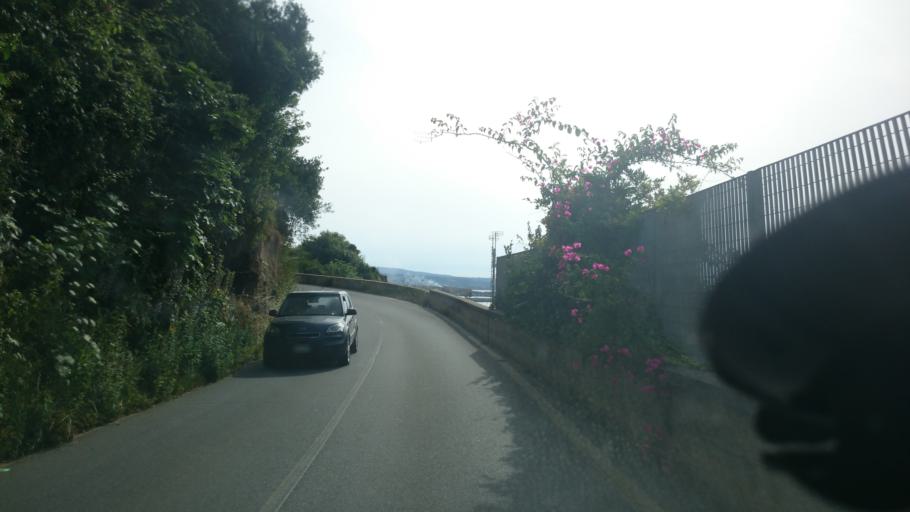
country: IT
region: Calabria
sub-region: Provincia di Vibo-Valentia
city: Sant'Onofrio
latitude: 38.7206
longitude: 16.1418
